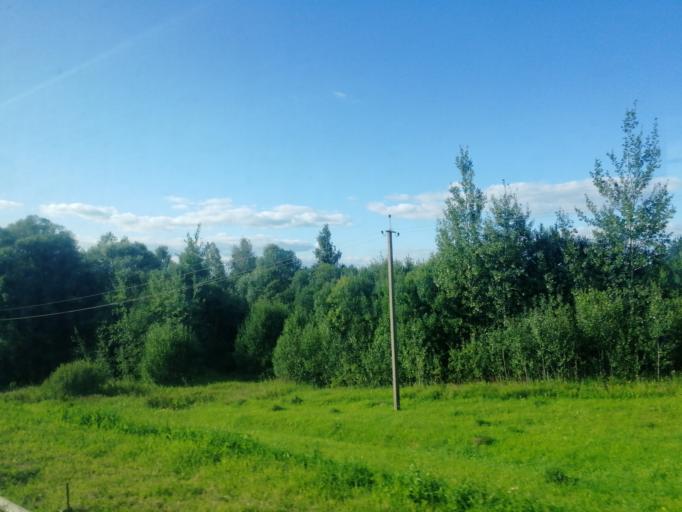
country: RU
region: Tula
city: Leninskiy
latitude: 54.2411
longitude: 37.3378
